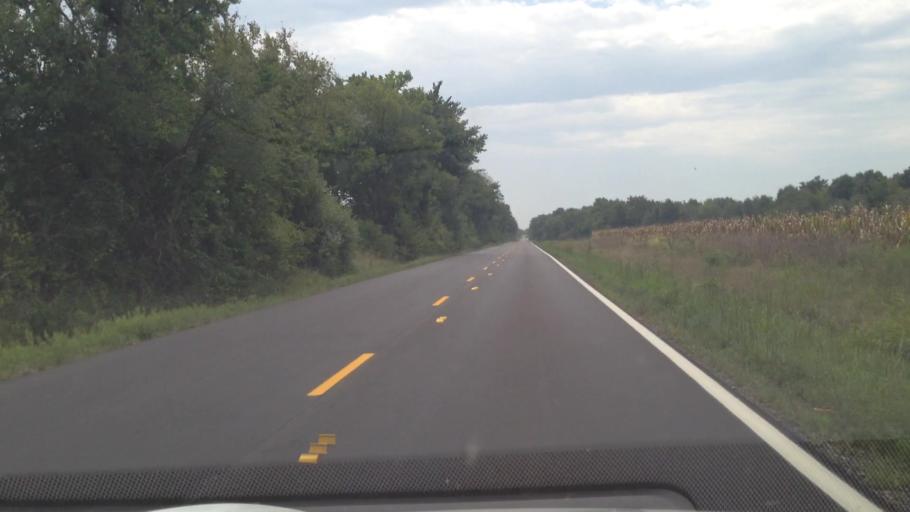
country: US
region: Kansas
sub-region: Crawford County
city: Girard
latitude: 37.5274
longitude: -94.9606
